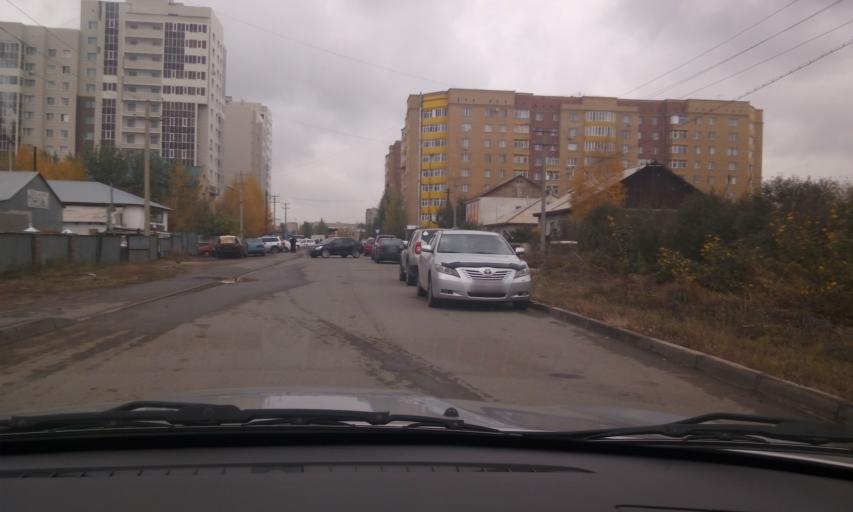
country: KZ
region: Astana Qalasy
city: Astana
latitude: 51.1394
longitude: 71.4863
